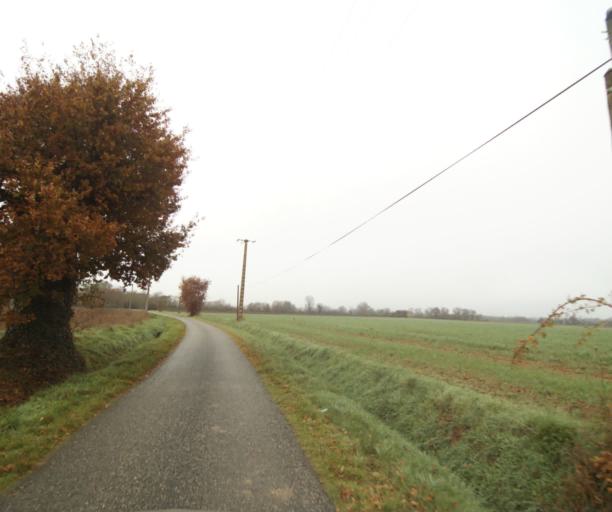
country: FR
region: Midi-Pyrenees
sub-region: Departement du Tarn-et-Garonne
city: Nohic
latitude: 43.8687
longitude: 1.4582
